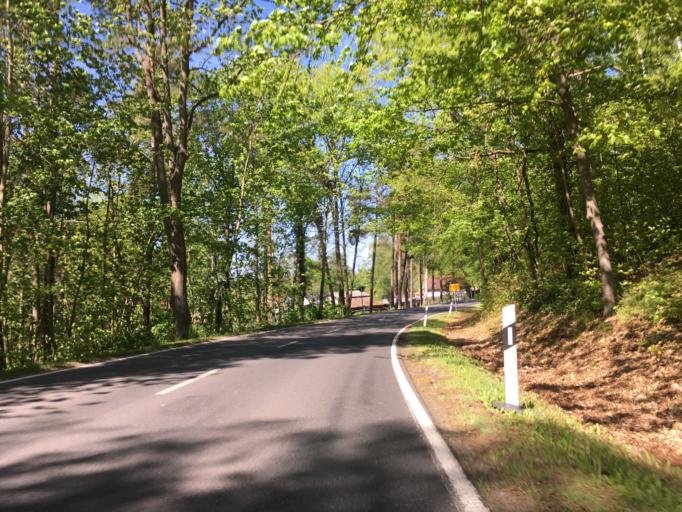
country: DE
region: Brandenburg
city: Marienwerder
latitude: 52.7865
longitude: 13.5551
